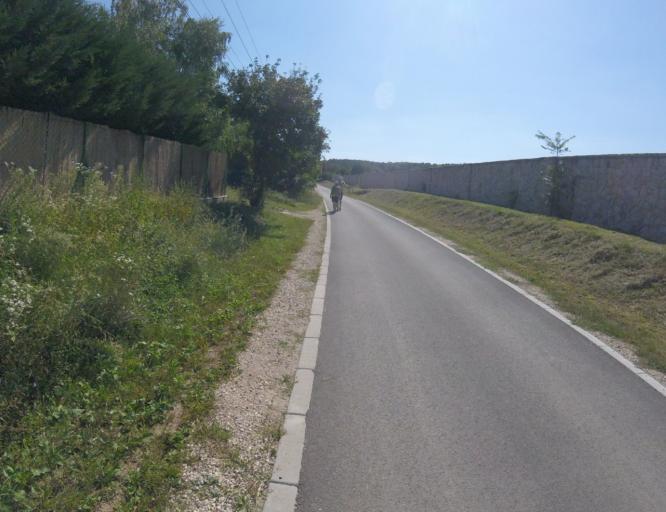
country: HU
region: Fejer
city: Velence
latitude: 47.2549
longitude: 18.6120
